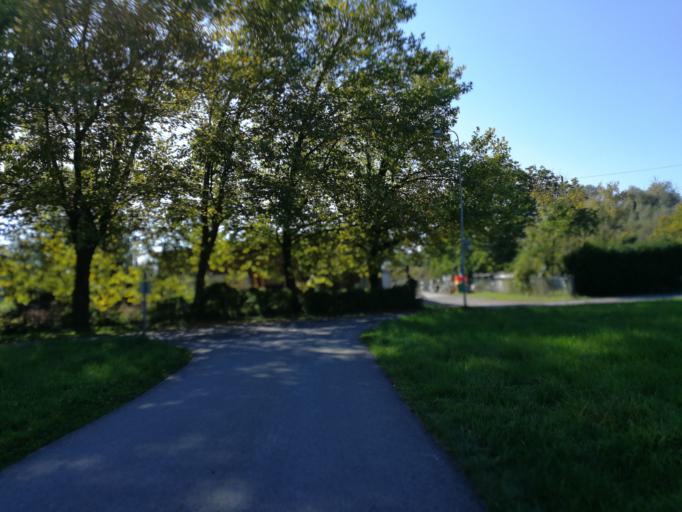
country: CH
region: Zurich
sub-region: Bezirk Meilen
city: Maennedorf / Ausserfeld
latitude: 47.2464
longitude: 8.7117
